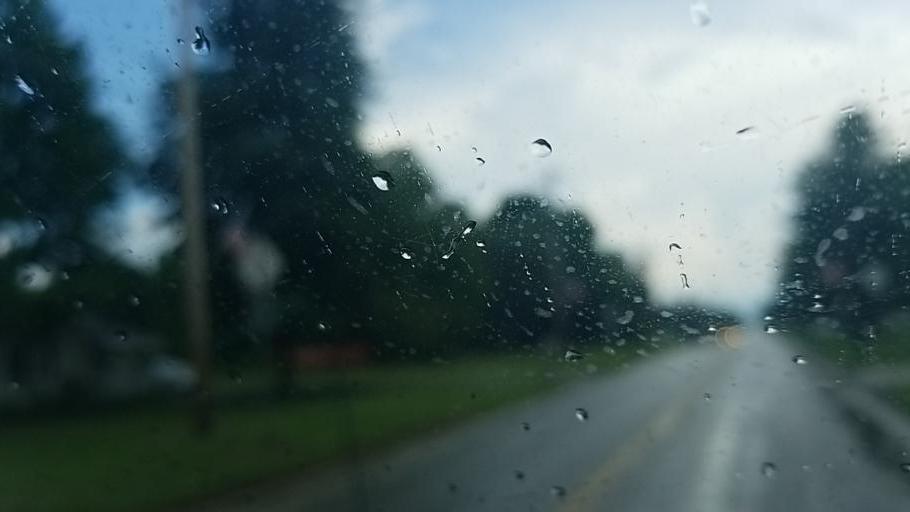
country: US
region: Ohio
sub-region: Lorain County
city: Grafton
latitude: 41.1679
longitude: -82.0203
